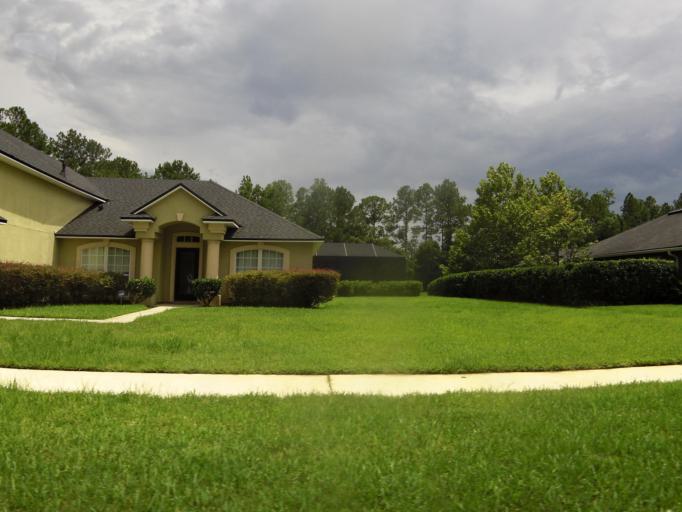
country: US
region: Florida
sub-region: Duval County
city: Jacksonville
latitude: 30.4235
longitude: -81.7255
